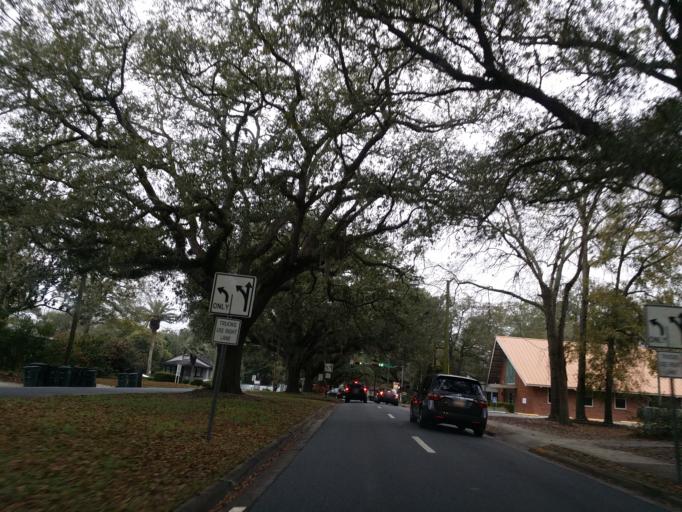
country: US
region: Florida
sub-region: Leon County
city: Tallahassee
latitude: 30.4579
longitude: -84.2834
